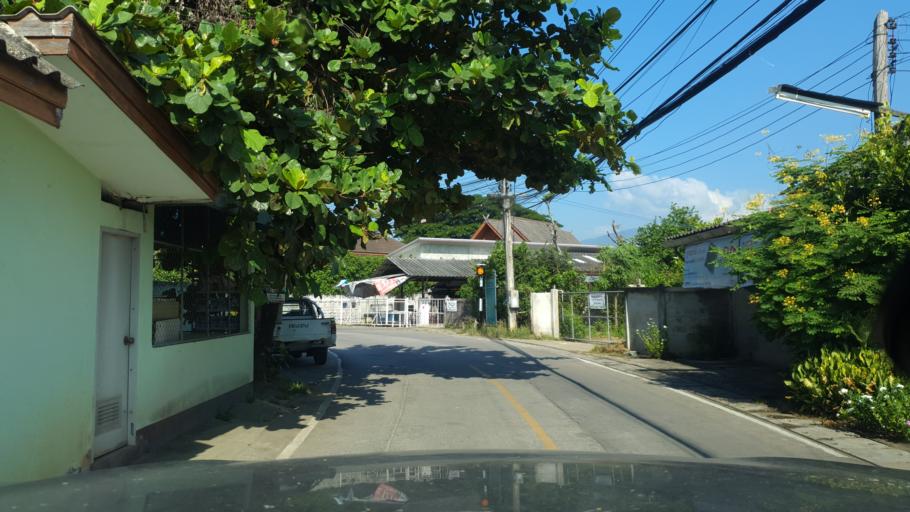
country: TH
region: Chiang Mai
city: Hang Dong
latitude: 18.7120
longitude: 98.9427
